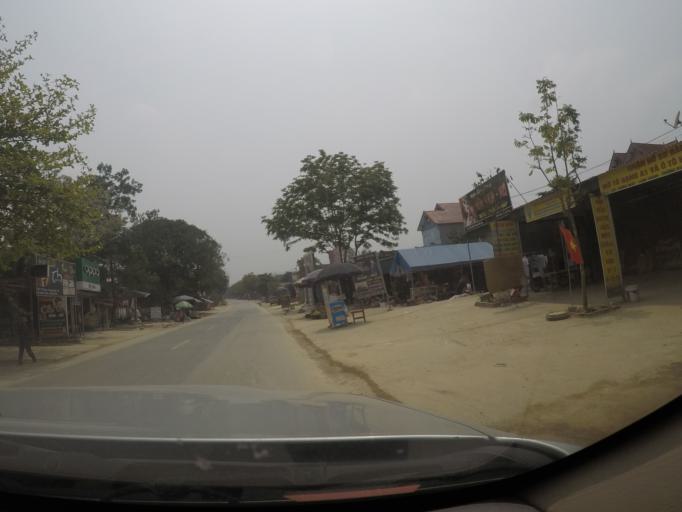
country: VN
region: Thanh Hoa
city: Thi Tran Thuong Xuan
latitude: 19.8059
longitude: 105.3955
